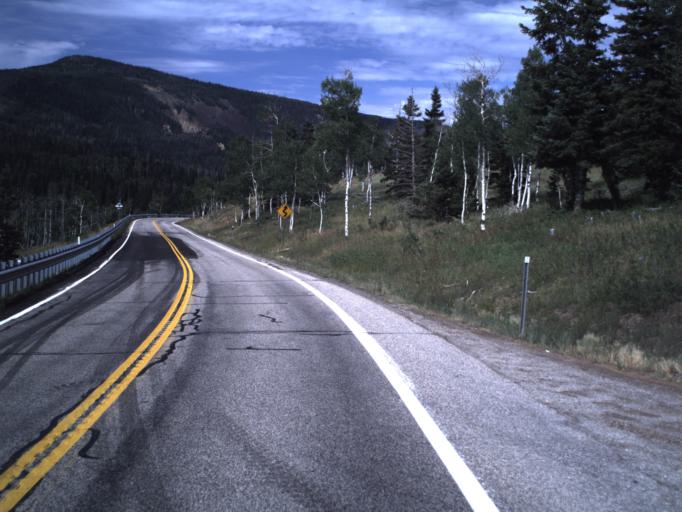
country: US
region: Utah
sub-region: Iron County
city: Cedar City
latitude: 37.5936
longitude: -112.8939
